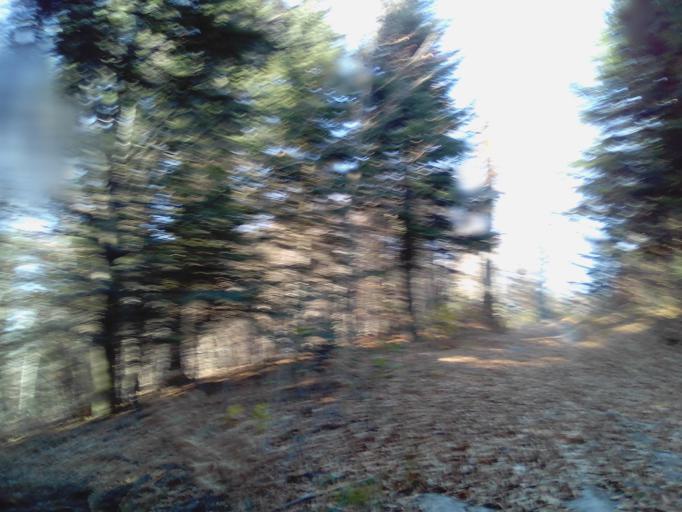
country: PL
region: Subcarpathian Voivodeship
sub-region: Powiat strzyzowski
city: Wysoka Strzyzowska
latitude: 49.8174
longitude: 21.7064
